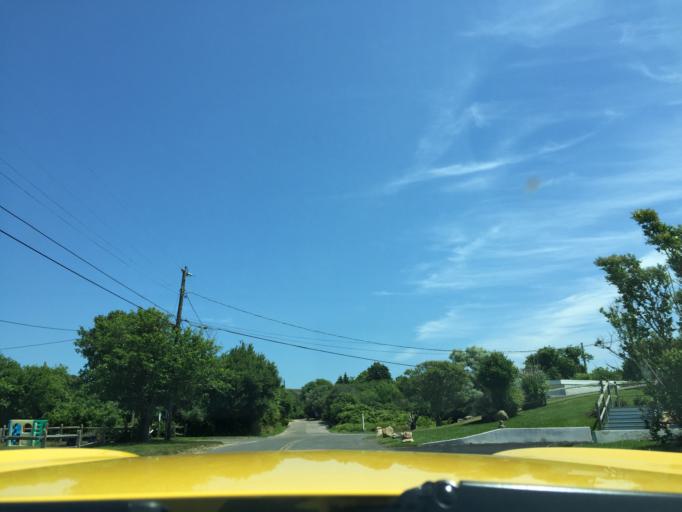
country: US
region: New York
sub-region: Suffolk County
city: Montauk
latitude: 41.0363
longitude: -71.9394
